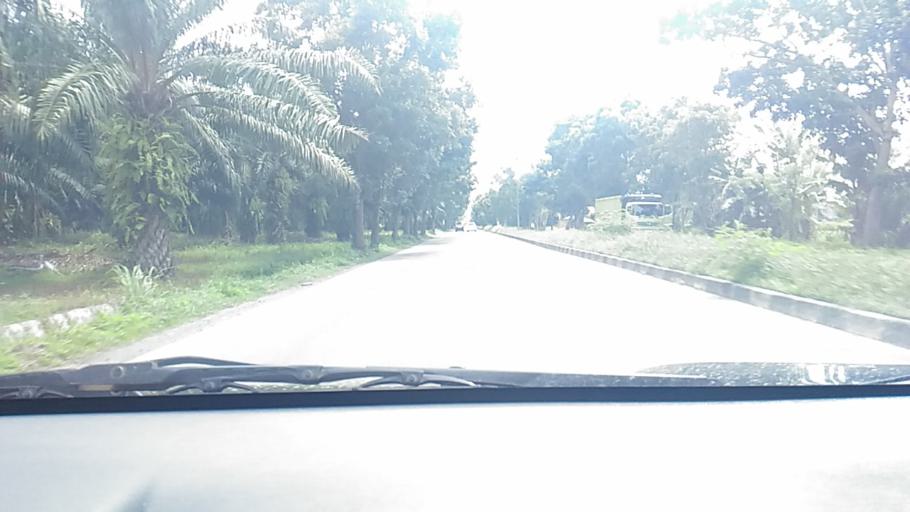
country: ID
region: North Sumatra
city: Binjai
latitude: 3.6505
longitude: 98.5159
